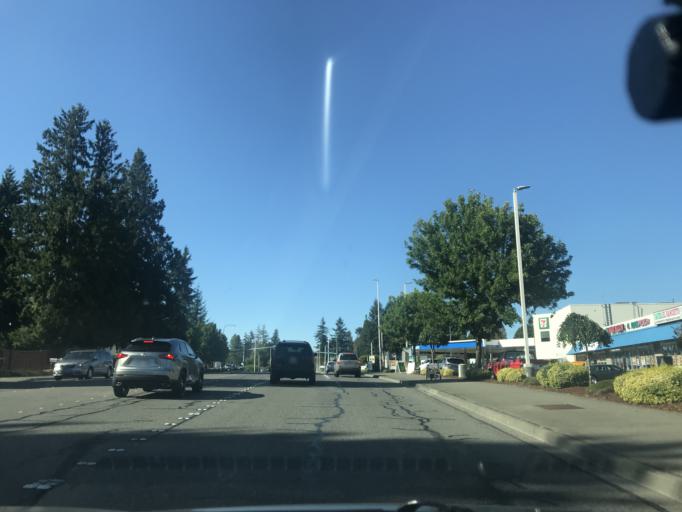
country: US
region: Washington
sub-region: King County
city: Lea Hill
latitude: 47.3655
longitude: -122.1867
